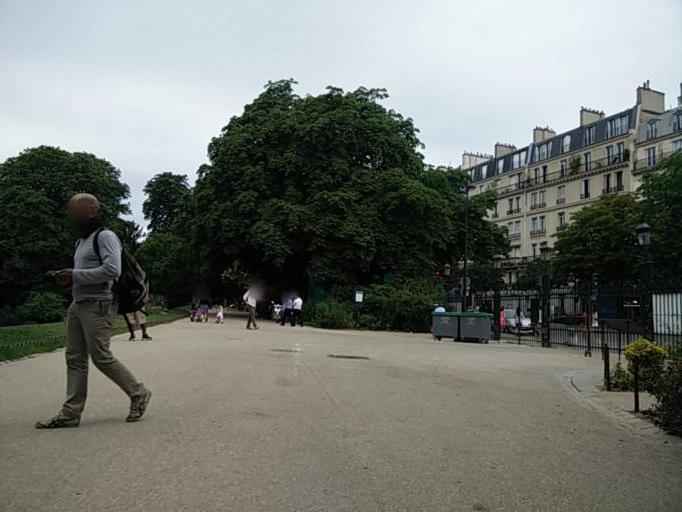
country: FR
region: Ile-de-France
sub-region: Departement de Seine-Saint-Denis
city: Le Pre-Saint-Gervais
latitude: 48.8822
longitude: 2.3824
